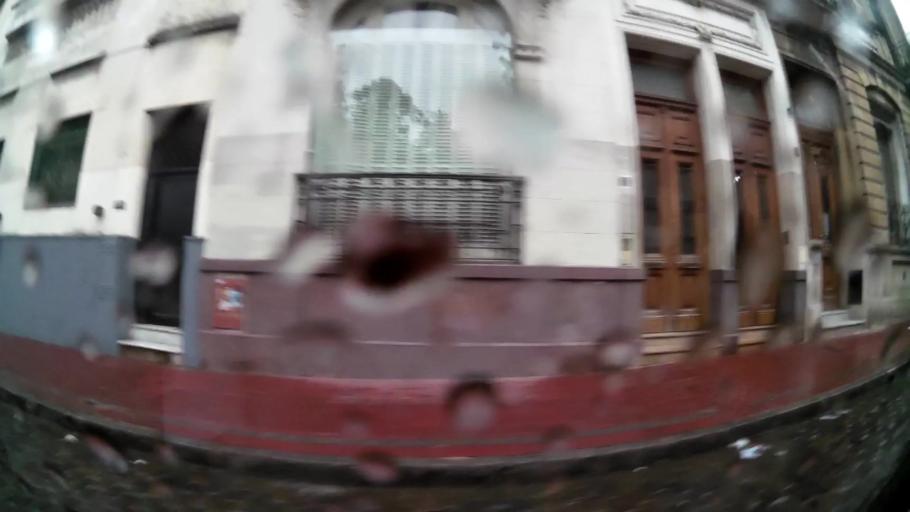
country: AR
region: Buenos Aires F.D.
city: Buenos Aires
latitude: -34.6263
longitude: -58.3710
